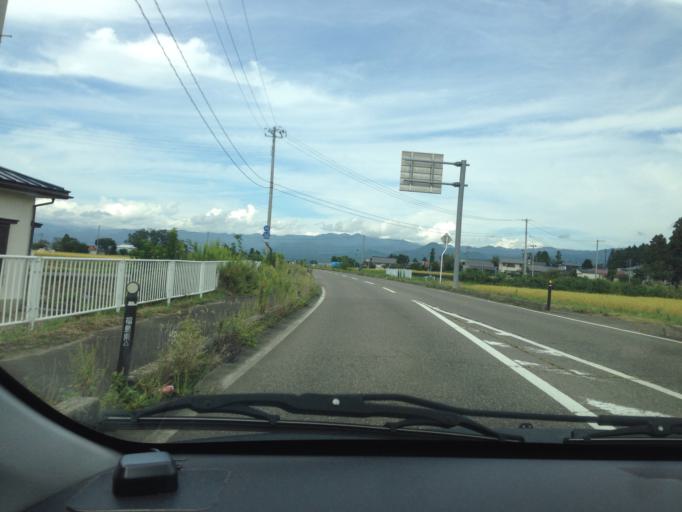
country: JP
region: Fukushima
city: Kitakata
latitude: 37.6110
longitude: 139.9124
